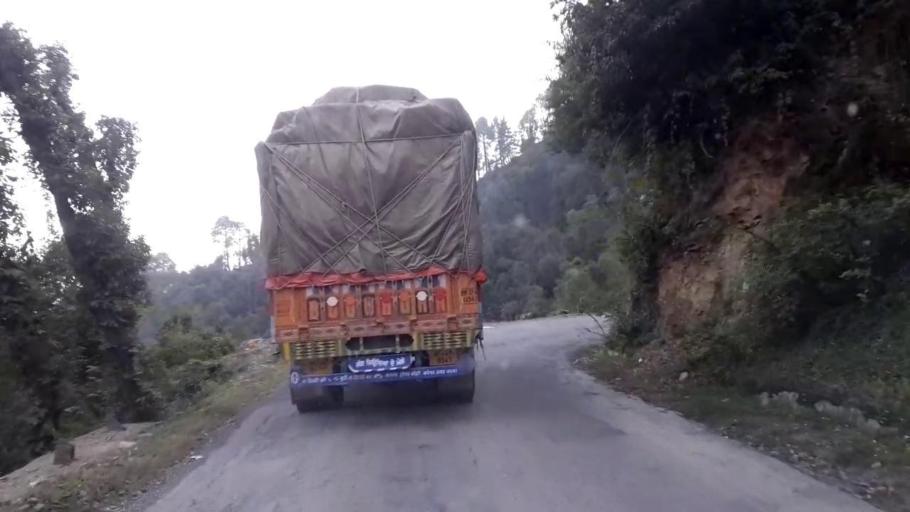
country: IN
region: Himachal Pradesh
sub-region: Shimla
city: Shimla
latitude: 31.0515
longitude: 77.1485
